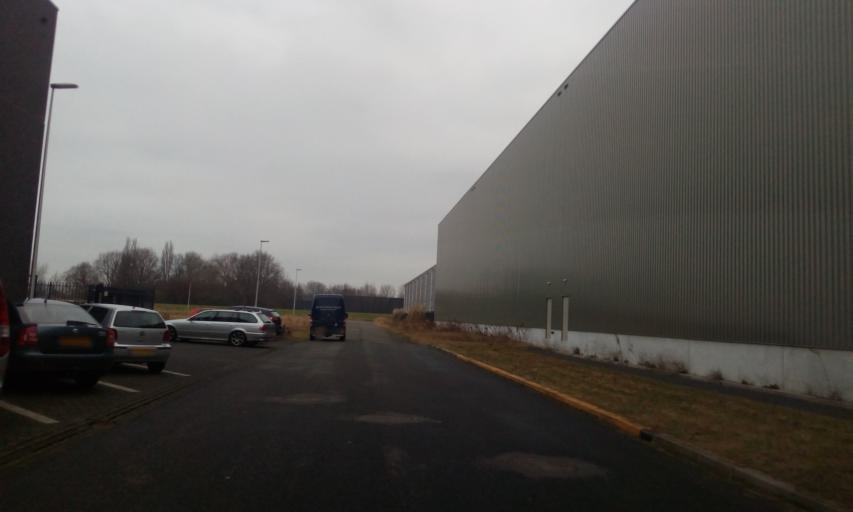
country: NL
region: South Holland
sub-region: Gemeente Lansingerland
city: Bleiswijk
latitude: 52.0447
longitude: 4.5351
